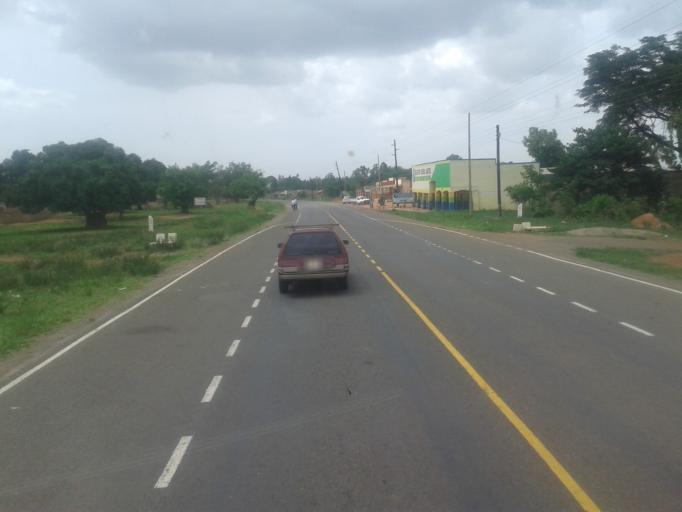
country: UG
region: Northern Region
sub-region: Oyam District
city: Oyam
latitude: 2.4637
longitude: 32.3779
